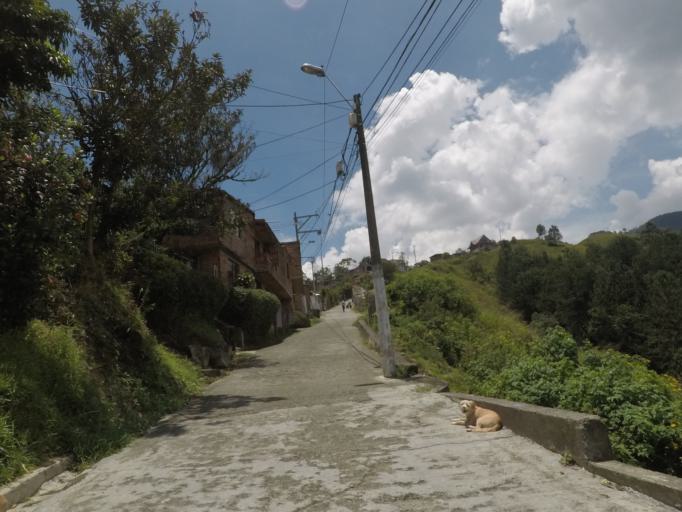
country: CO
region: Antioquia
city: Medellin
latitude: 6.2724
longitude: -75.6371
